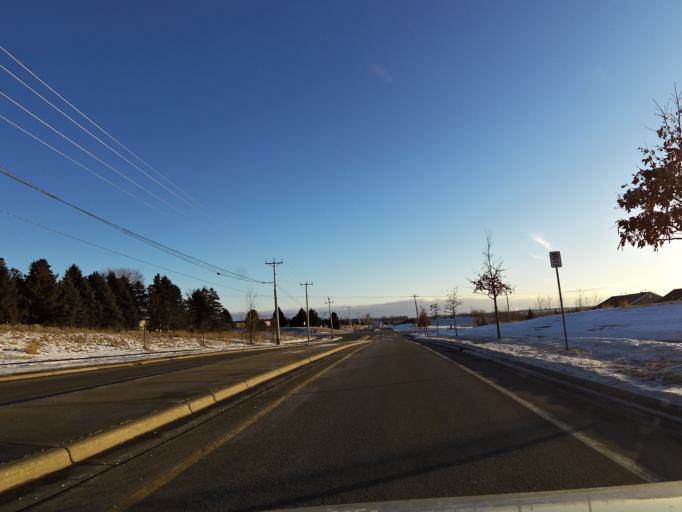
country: US
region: Minnesota
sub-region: Washington County
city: Woodbury
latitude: 44.8924
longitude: -92.8831
